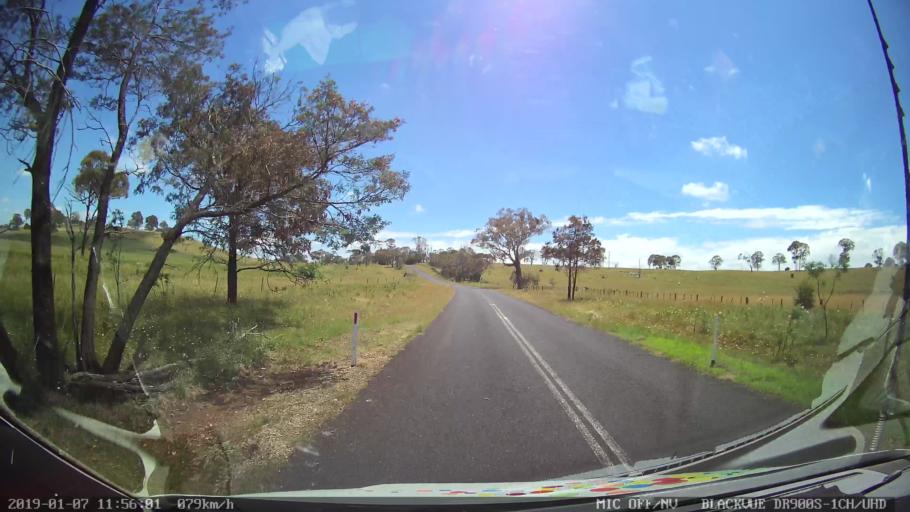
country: AU
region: New South Wales
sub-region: Guyra
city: Guyra
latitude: -30.2793
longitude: 151.6734
